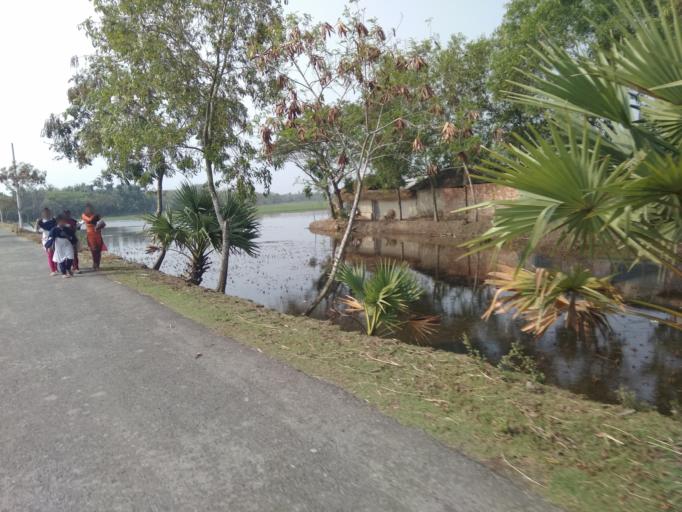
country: IN
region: West Bengal
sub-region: North 24 Parganas
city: Gosaba
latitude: 22.2593
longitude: 89.1152
